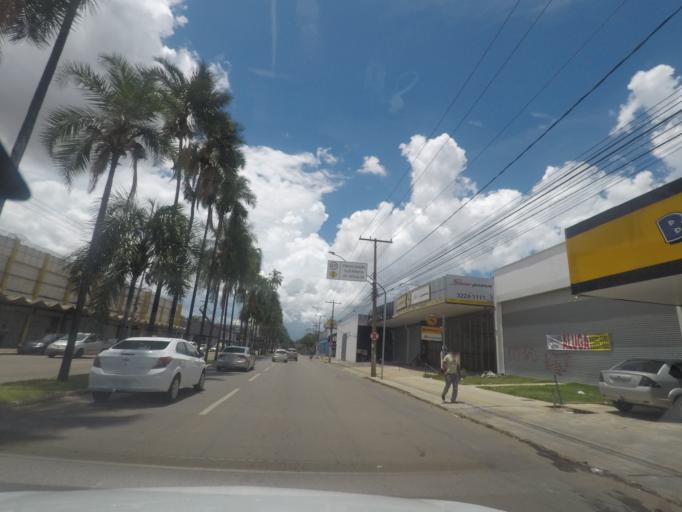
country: BR
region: Goias
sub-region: Goiania
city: Goiania
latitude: -16.6634
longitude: -49.2582
